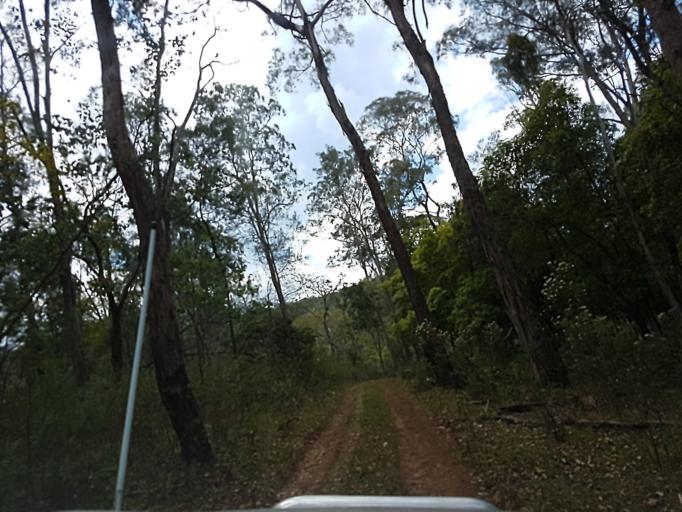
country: AU
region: Victoria
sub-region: East Gippsland
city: Lakes Entrance
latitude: -37.3633
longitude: 148.3521
